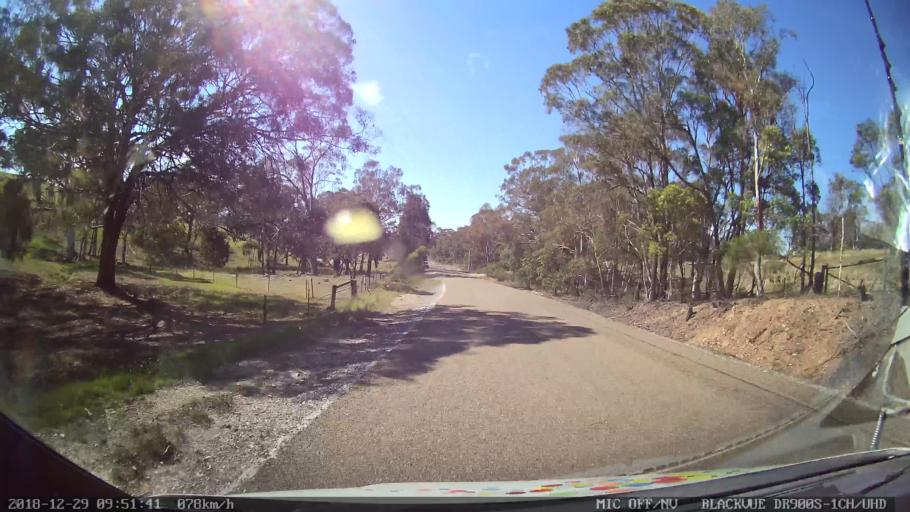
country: AU
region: New South Wales
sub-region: Goulburn Mulwaree
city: Goulburn
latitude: -34.7349
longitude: 149.4613
